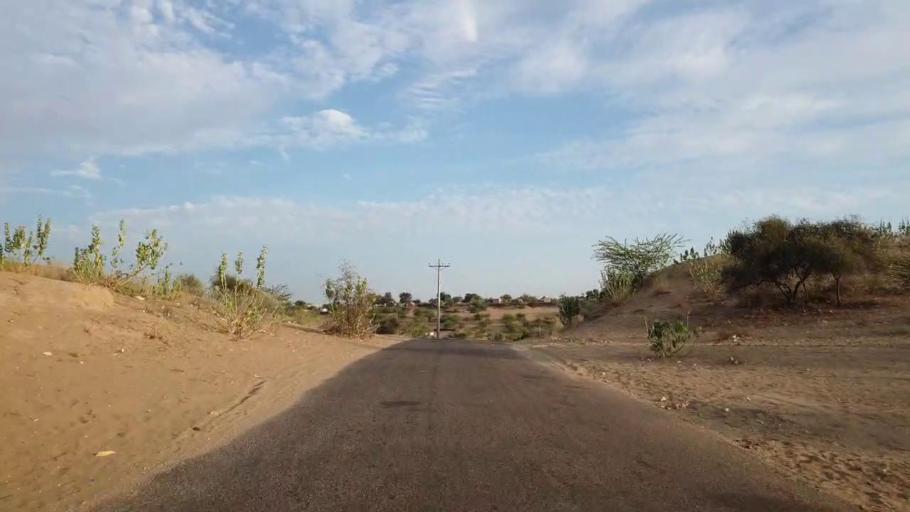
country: PK
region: Sindh
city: Umarkot
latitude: 25.1585
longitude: 70.0102
